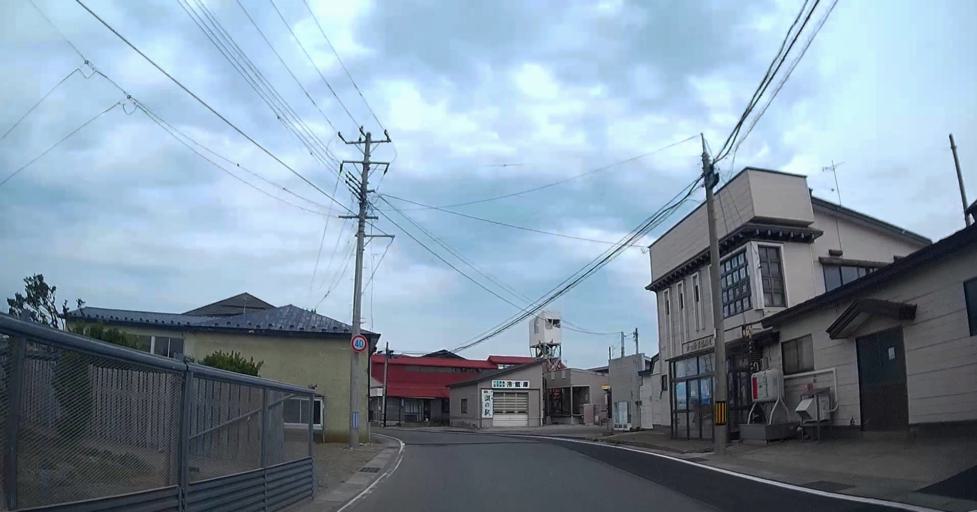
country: JP
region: Aomori
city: Shimokizukuri
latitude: 41.0362
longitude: 140.3294
